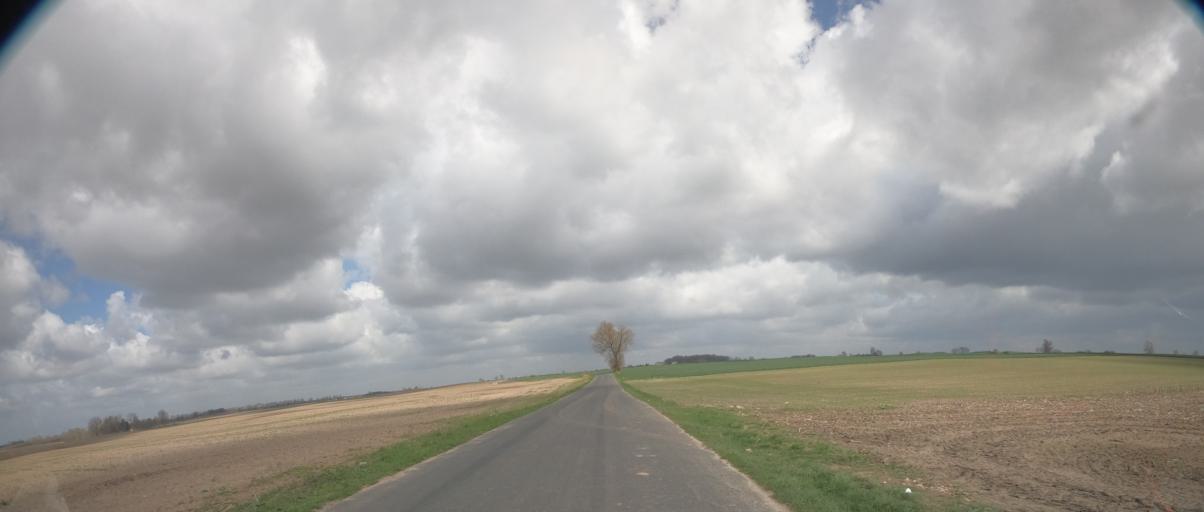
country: PL
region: West Pomeranian Voivodeship
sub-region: Powiat choszczenski
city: Recz
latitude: 53.2726
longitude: 15.4955
